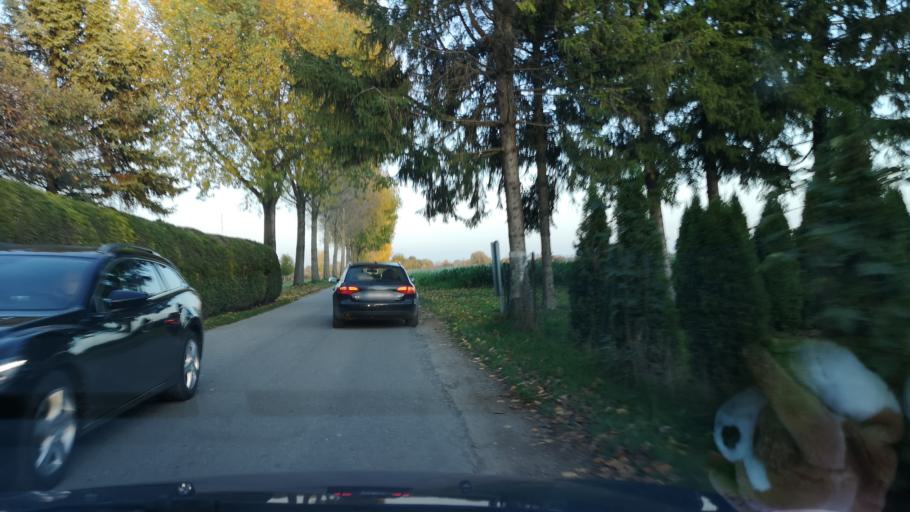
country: DE
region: Bavaria
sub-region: Upper Bavaria
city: Ismaning
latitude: 48.2450
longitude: 11.7219
